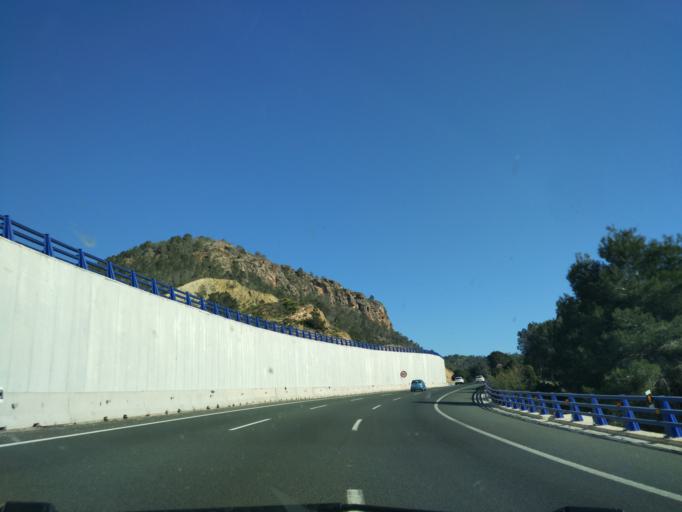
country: ES
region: Murcia
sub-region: Murcia
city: Murcia
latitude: 37.9052
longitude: -1.1470
